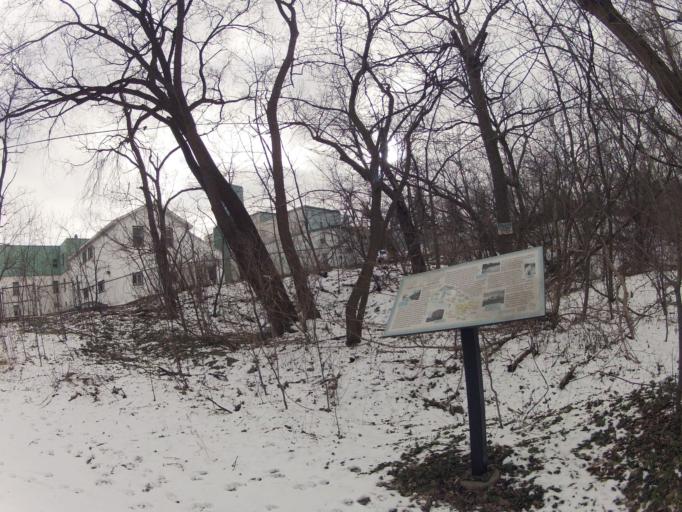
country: CA
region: Ontario
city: Mississauga
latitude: 43.5745
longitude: -79.6951
